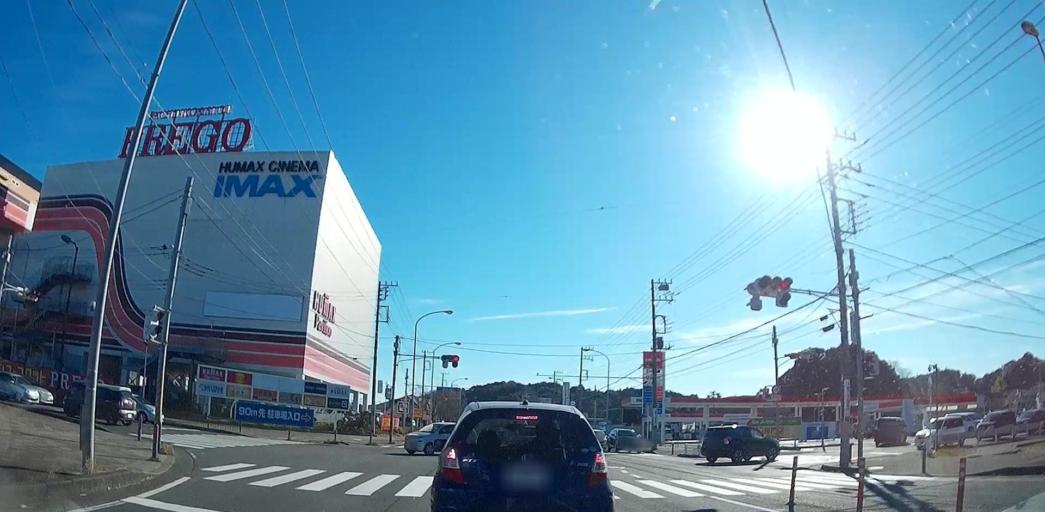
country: JP
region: Chiba
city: Narita
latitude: 35.7933
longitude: 140.3207
